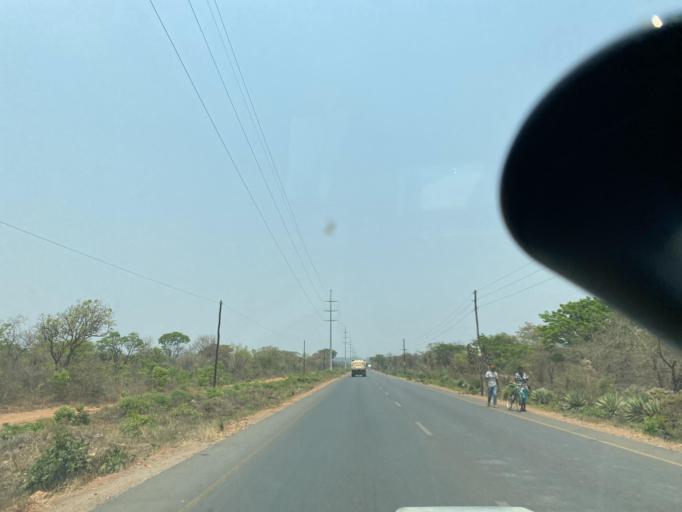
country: ZM
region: Lusaka
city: Lusaka
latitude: -15.5141
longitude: 28.4522
